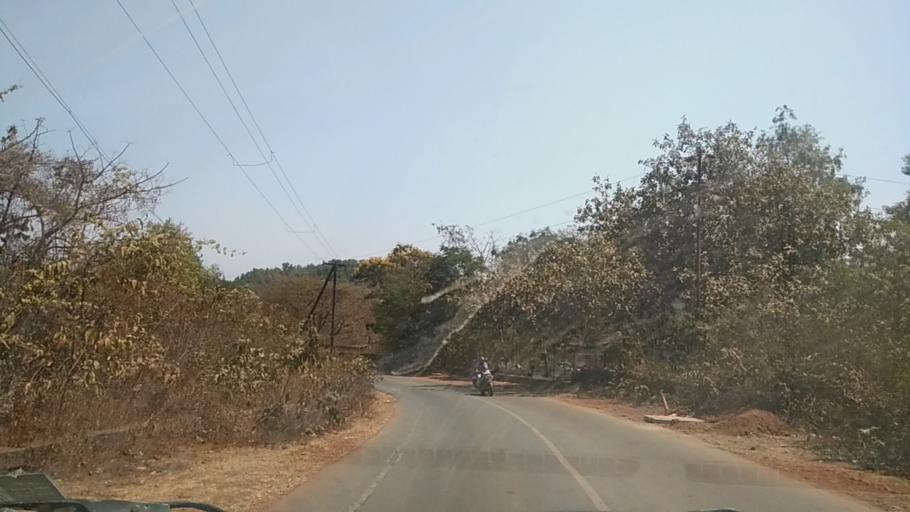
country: IN
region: Goa
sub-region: North Goa
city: Dicholi
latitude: 15.5820
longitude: 73.9375
